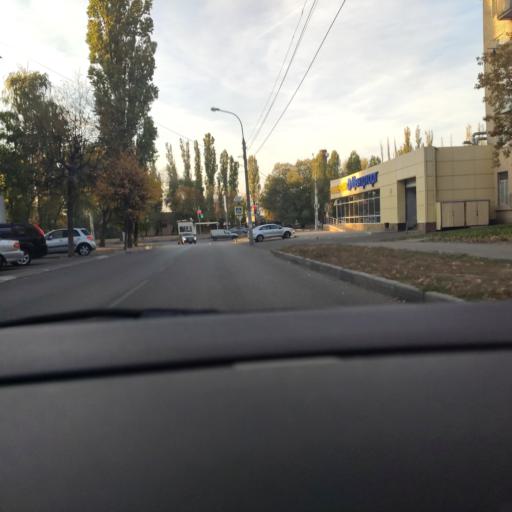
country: RU
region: Voronezj
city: Voronezh
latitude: 51.6573
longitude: 39.1454
